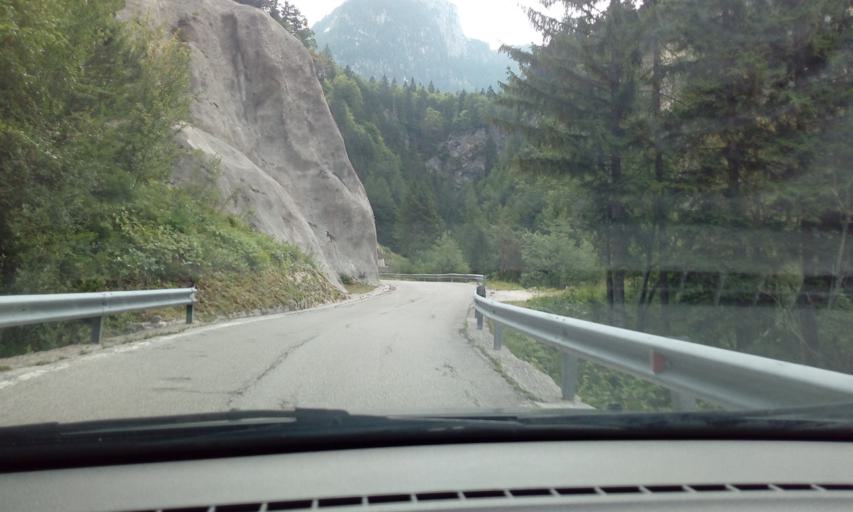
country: SI
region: Bovec
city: Bovec
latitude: 46.3909
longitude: 13.4667
